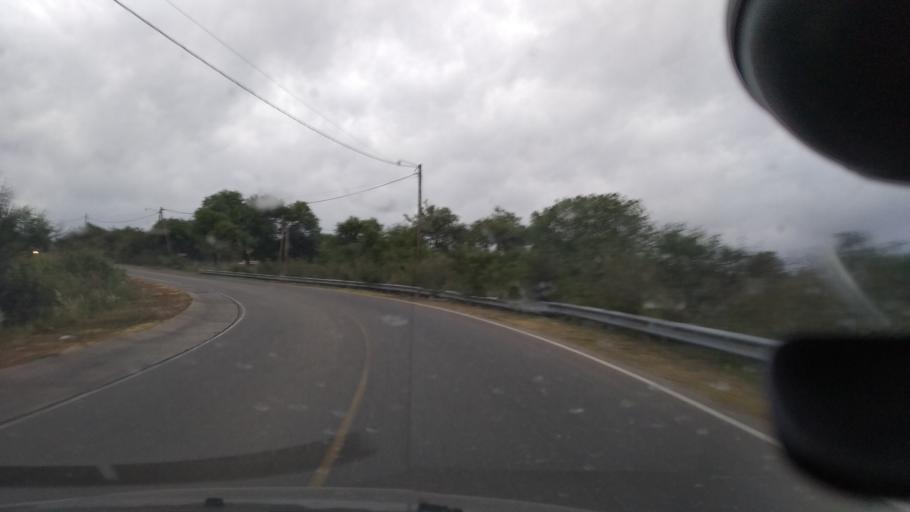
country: AR
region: Cordoba
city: Villa Las Rosas
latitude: -31.9291
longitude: -65.0368
